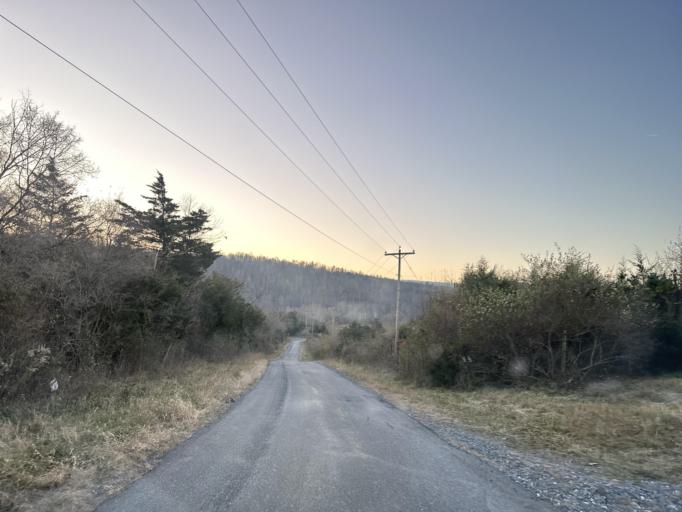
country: US
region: Virginia
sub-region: Augusta County
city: Jolivue
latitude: 38.0825
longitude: -79.3662
